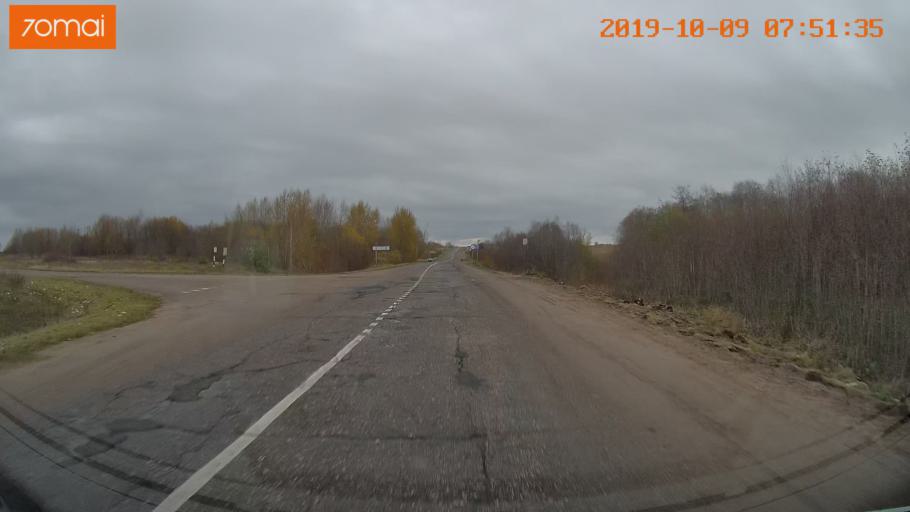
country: RU
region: Jaroslavl
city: Kukoboy
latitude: 58.6842
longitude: 39.8798
